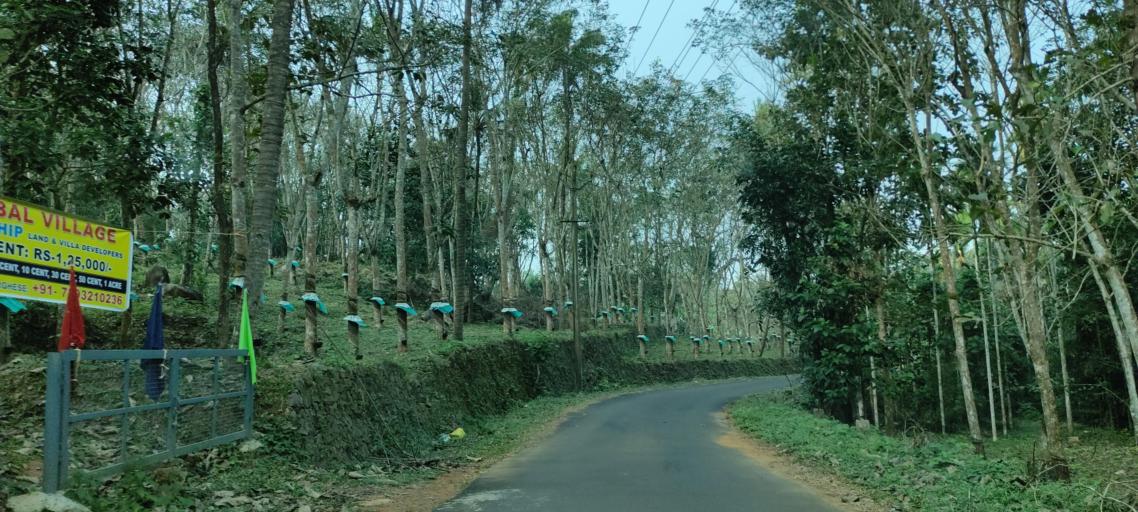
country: IN
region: Kerala
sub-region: Ernakulam
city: Piravam
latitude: 9.8115
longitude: 76.5249
